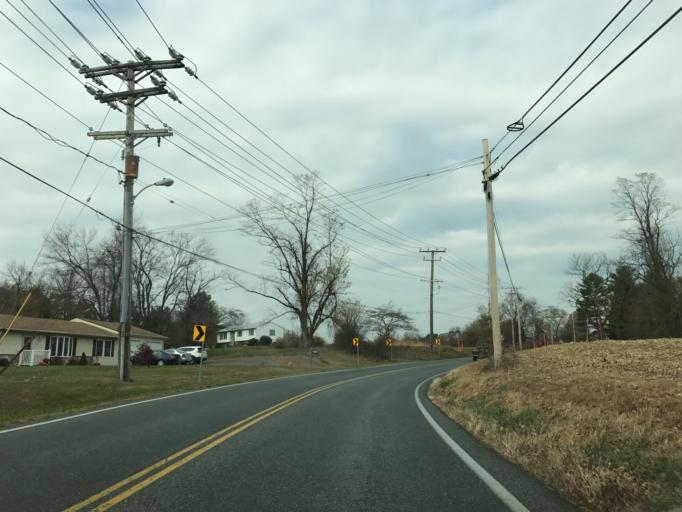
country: US
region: Maryland
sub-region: Harford County
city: Jarrettsville
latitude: 39.5830
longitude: -76.4279
